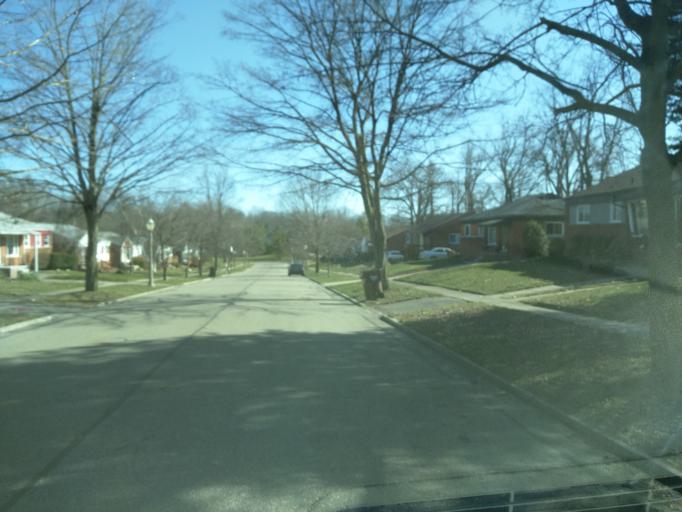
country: US
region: Michigan
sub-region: Ingham County
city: Edgemont Park
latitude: 42.7577
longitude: -84.5867
